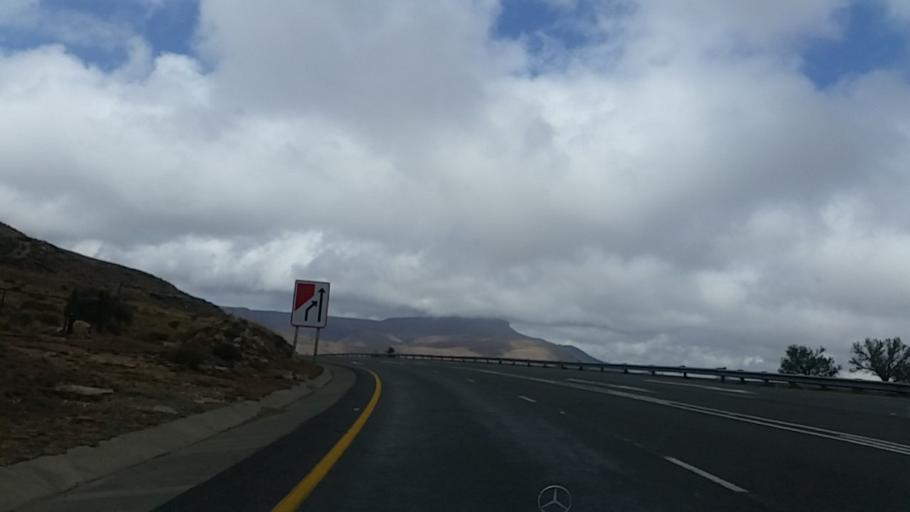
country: ZA
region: Eastern Cape
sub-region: Chris Hani District Municipality
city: Middelburg
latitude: -31.8360
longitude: 24.8589
